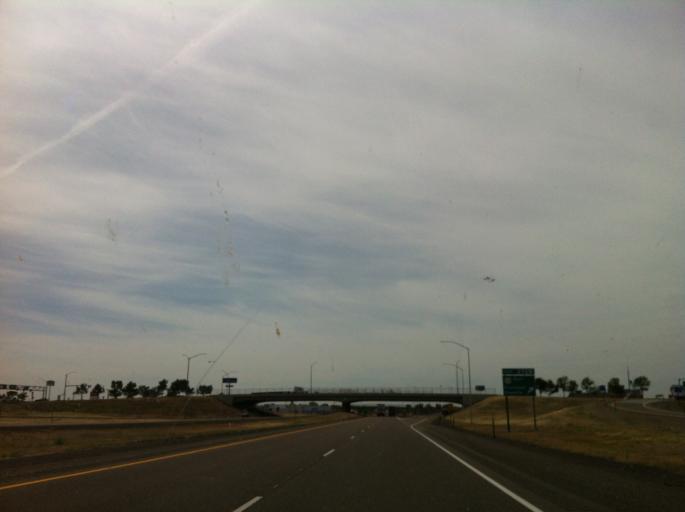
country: US
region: Oregon
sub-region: Malheur County
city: Ontario
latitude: 44.0321
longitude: -116.9526
